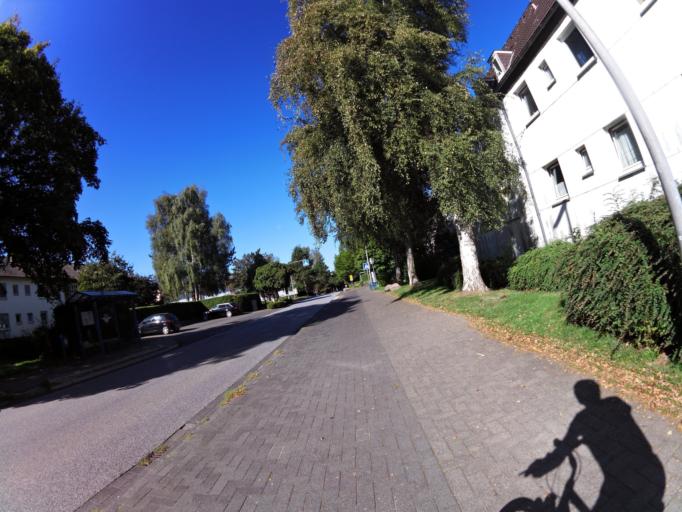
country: DE
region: Schleswig-Holstein
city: Barkelsby
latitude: 54.4852
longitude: 9.8278
